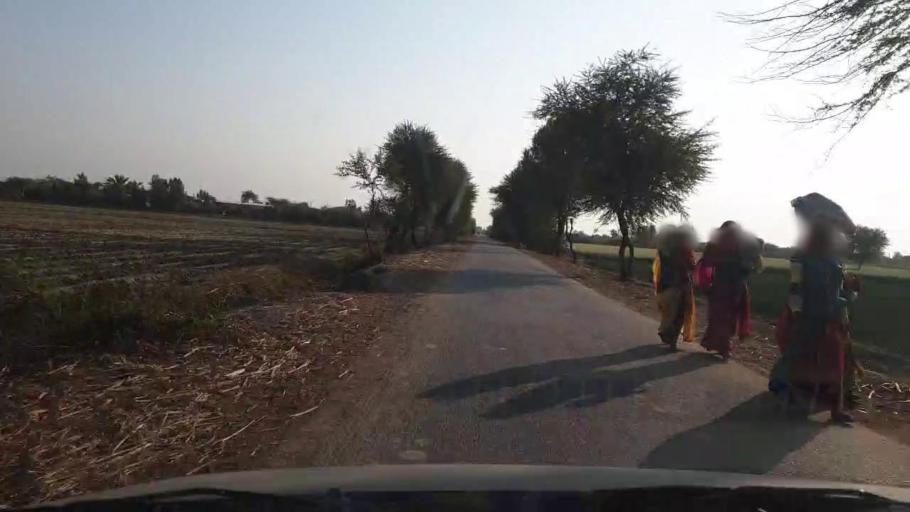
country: PK
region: Sindh
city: Samaro
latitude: 25.2666
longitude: 69.3604
